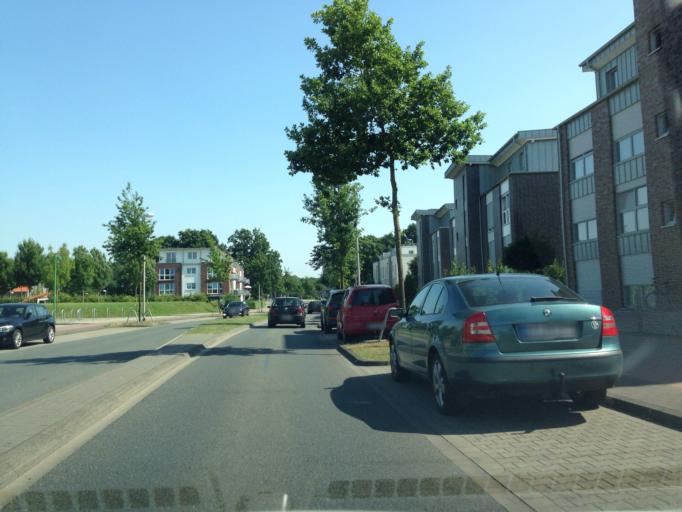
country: DE
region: North Rhine-Westphalia
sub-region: Regierungsbezirk Munster
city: Muenster
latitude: 51.9610
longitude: 7.5681
